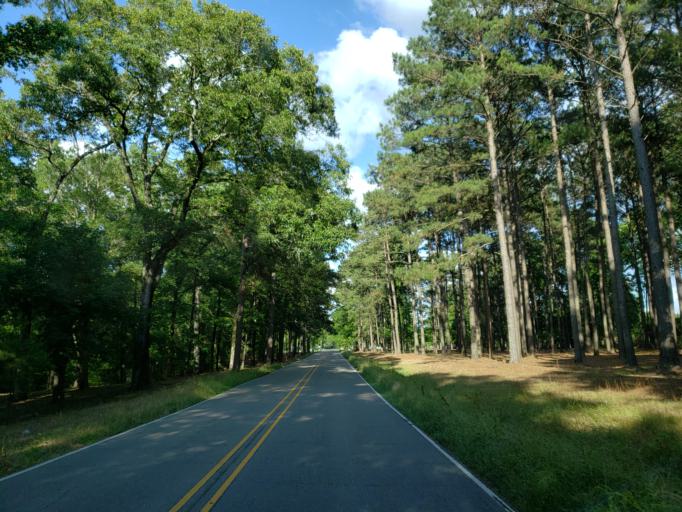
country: US
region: Mississippi
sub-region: Forrest County
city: Petal
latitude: 31.3202
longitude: -89.2026
